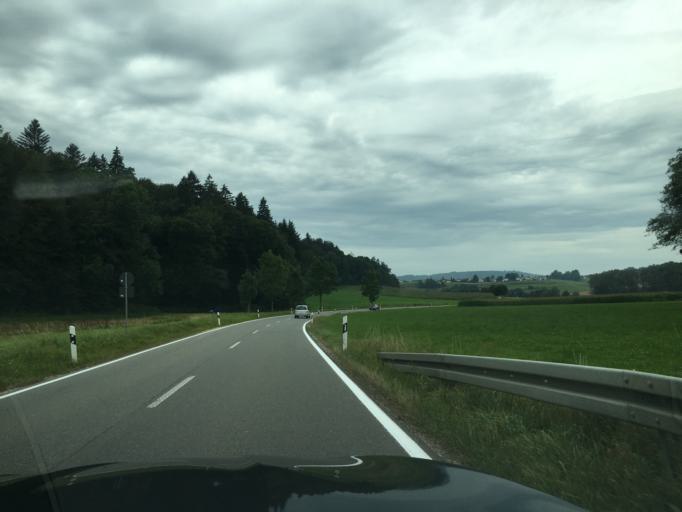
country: DE
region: Baden-Wuerttemberg
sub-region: Freiburg Region
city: Stockach
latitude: 47.8547
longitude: 9.0407
